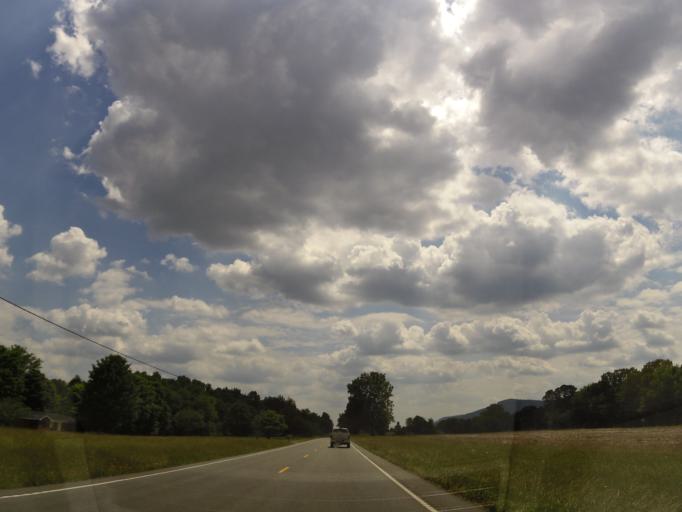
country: US
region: Tennessee
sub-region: Sequatchie County
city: Dunlap
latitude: 35.4303
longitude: -85.3534
